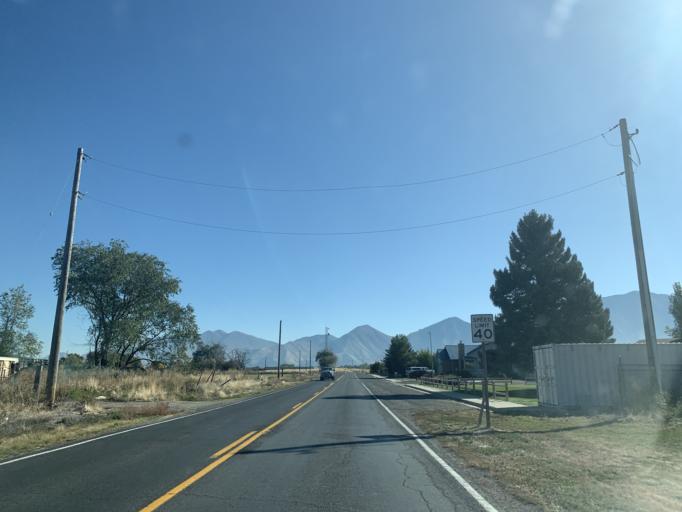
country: US
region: Utah
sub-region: Utah County
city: West Mountain
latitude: 40.0411
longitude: -111.7653
